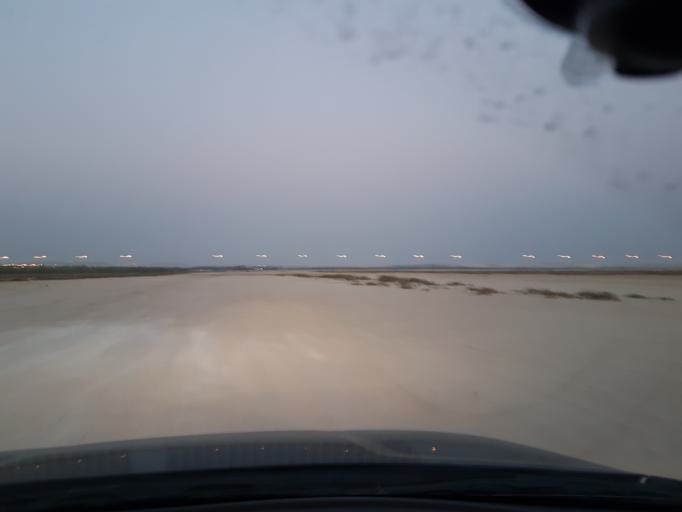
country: BH
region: Central Governorate
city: Dar Kulayb
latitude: 26.0099
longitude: 50.4781
